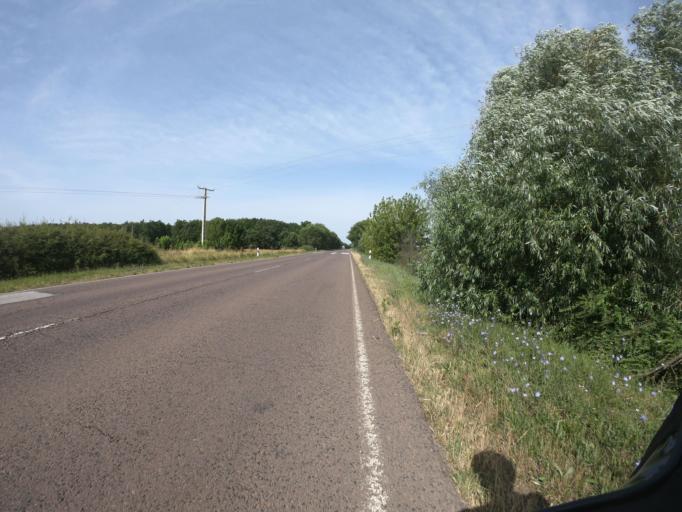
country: HU
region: Hajdu-Bihar
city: Egyek
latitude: 47.5936
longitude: 20.8435
